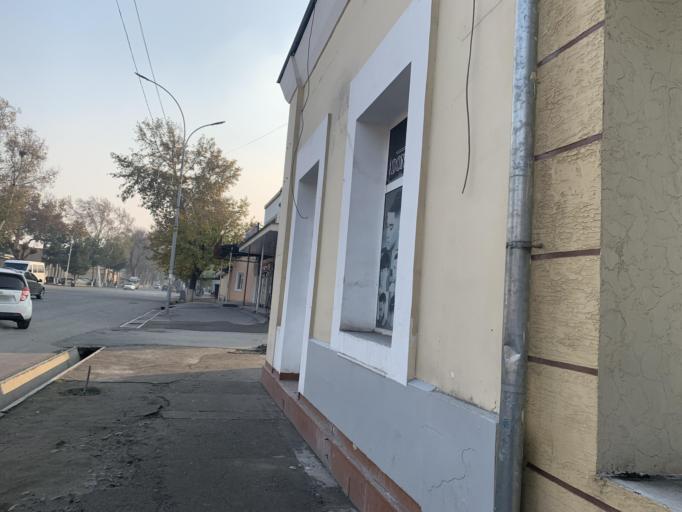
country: UZ
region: Fergana
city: Qo`qon
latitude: 40.5345
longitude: 70.9374
